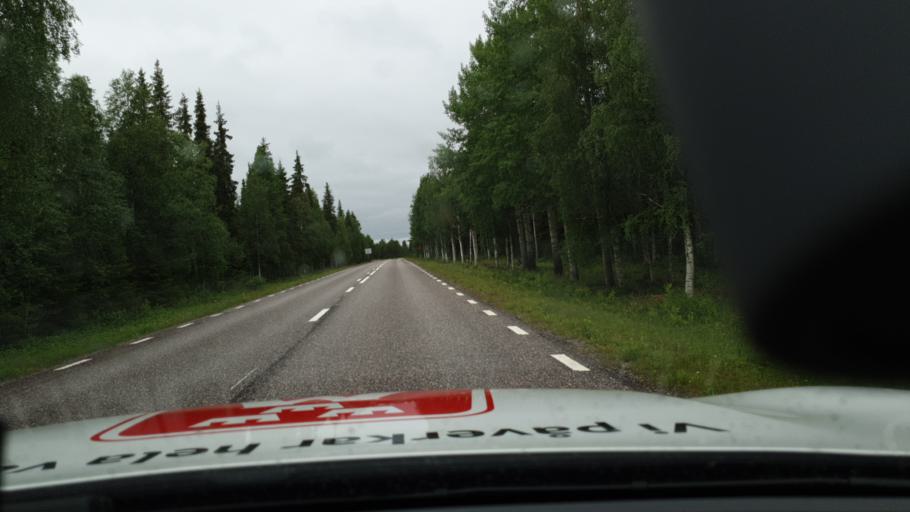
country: SE
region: Norrbotten
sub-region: Pajala Kommun
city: Pajala
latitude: 67.1919
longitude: 23.4693
